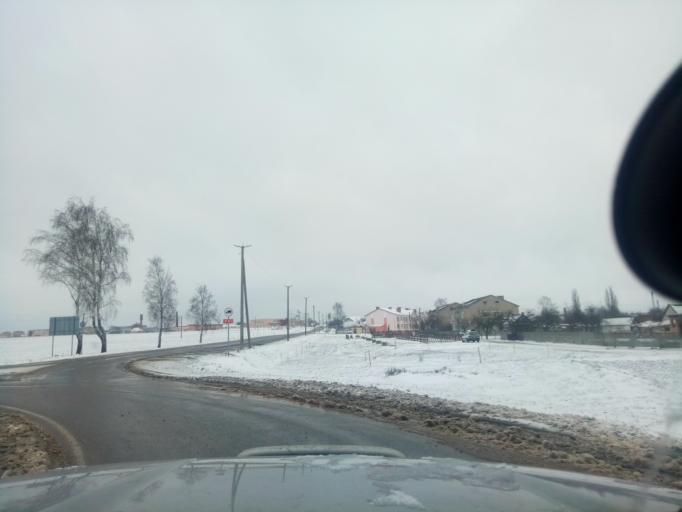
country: BY
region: Minsk
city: Kapyl'
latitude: 53.1375
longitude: 27.0874
